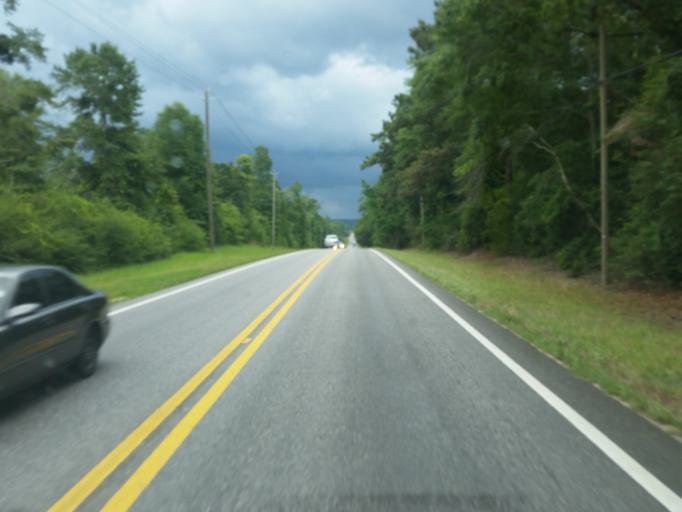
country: US
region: Mississippi
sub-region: Jackson County
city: Hurley
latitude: 30.8177
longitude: -88.3492
